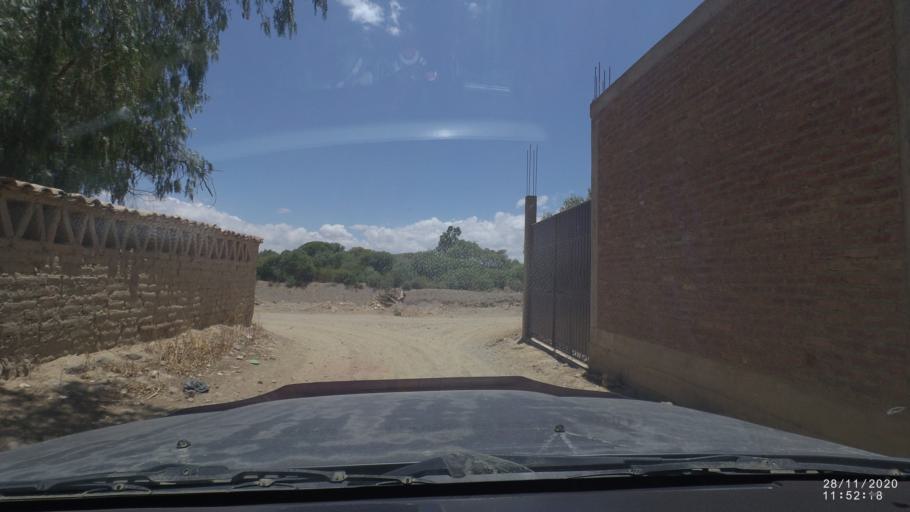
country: BO
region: Cochabamba
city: Tarata
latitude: -17.6166
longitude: -66.0220
